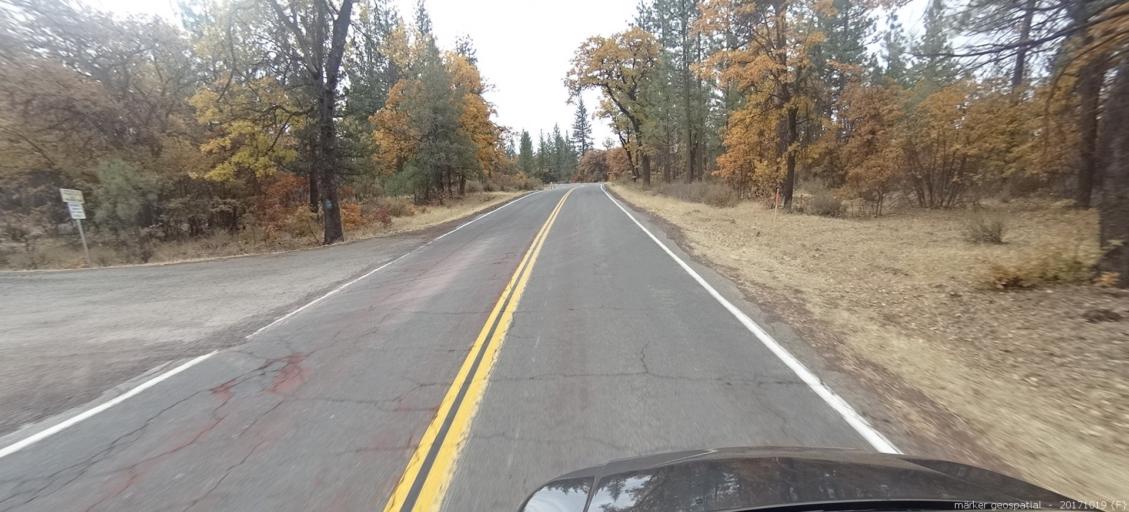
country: US
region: California
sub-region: Shasta County
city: Burney
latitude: 41.1151
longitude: -121.3318
